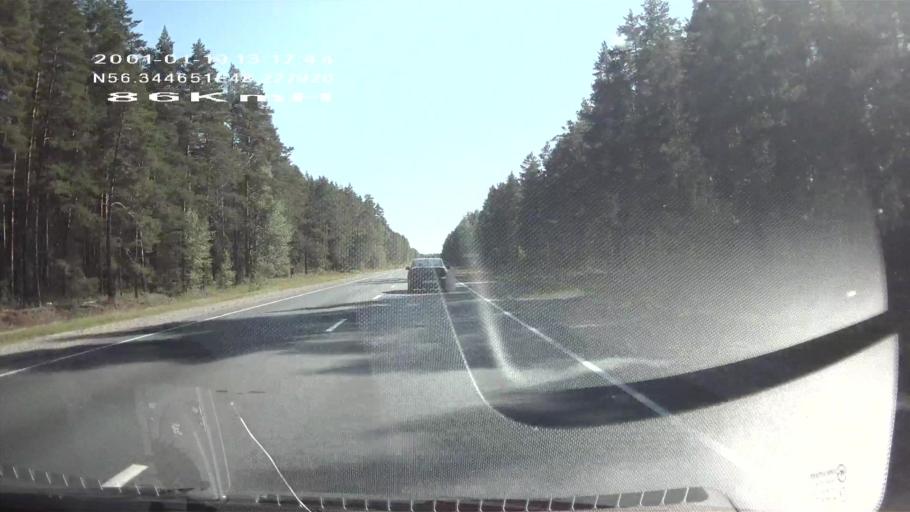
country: RU
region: Mariy-El
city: Suslonger
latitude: 56.3445
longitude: 48.2280
